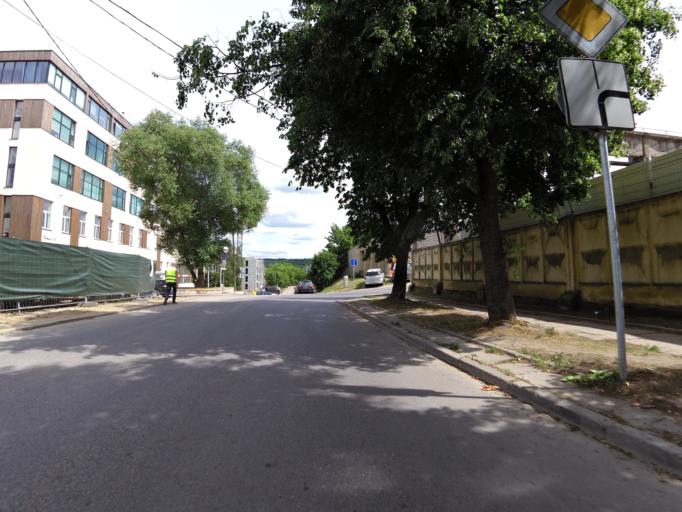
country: LT
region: Vilnius County
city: Rasos
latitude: 54.6773
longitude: 25.3180
